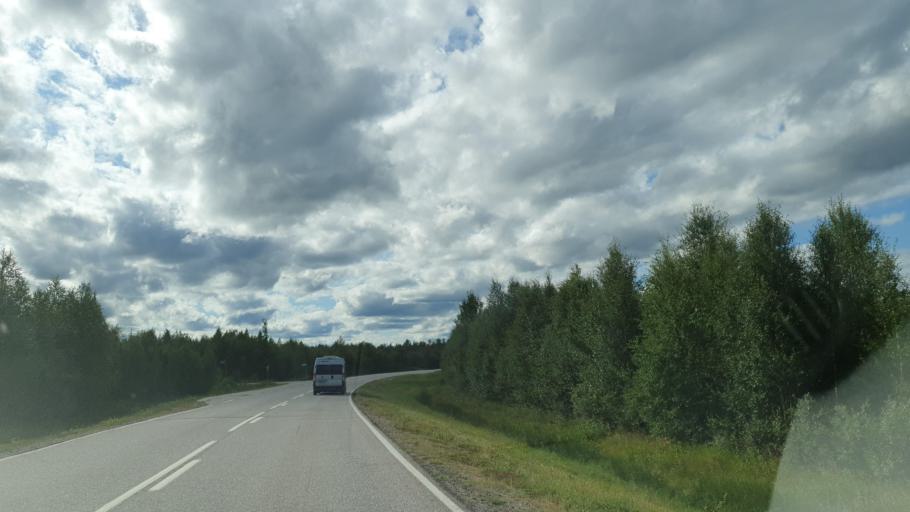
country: FI
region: Lapland
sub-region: Tunturi-Lappi
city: Muonio
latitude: 67.8614
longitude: 24.1545
